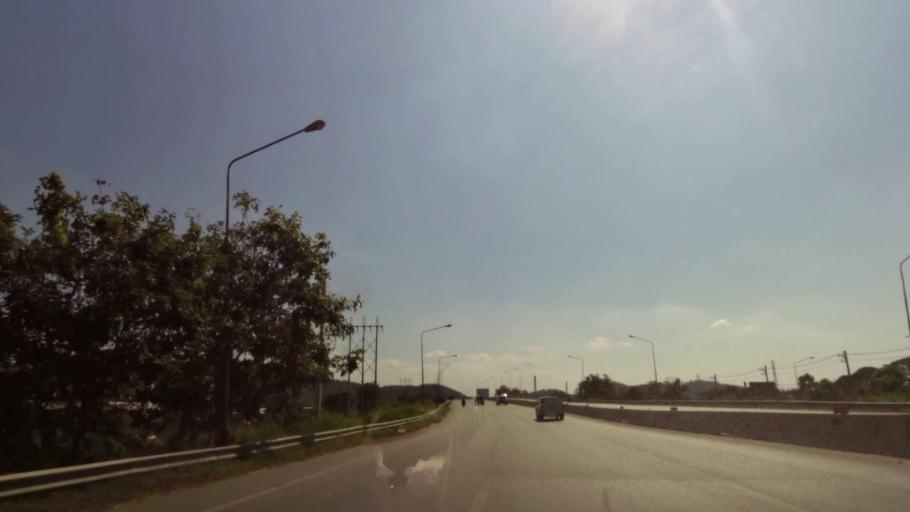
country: TH
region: Nakhon Sawan
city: Nakhon Sawan
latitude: 15.7309
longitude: 100.1173
